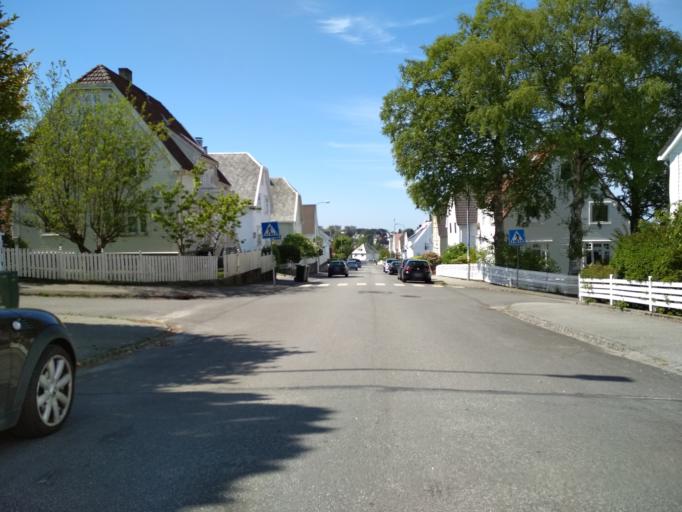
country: NO
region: Rogaland
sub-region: Stavanger
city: Stavanger
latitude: 58.9590
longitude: 5.7291
